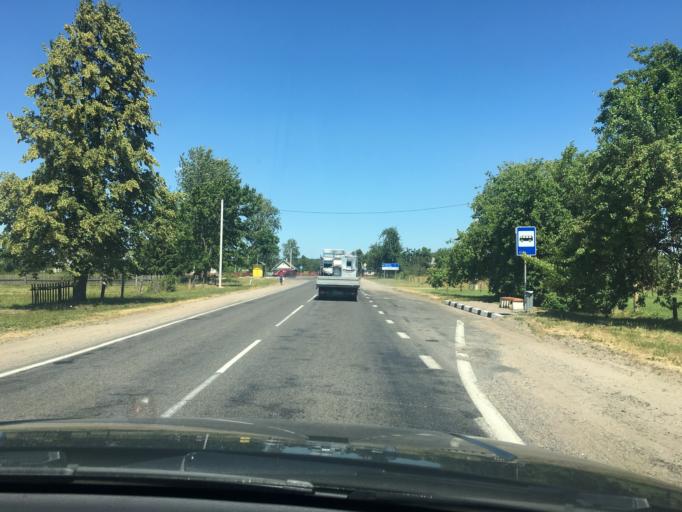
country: BY
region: Grodnenskaya
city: Iwye
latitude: 54.0636
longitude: 25.9108
